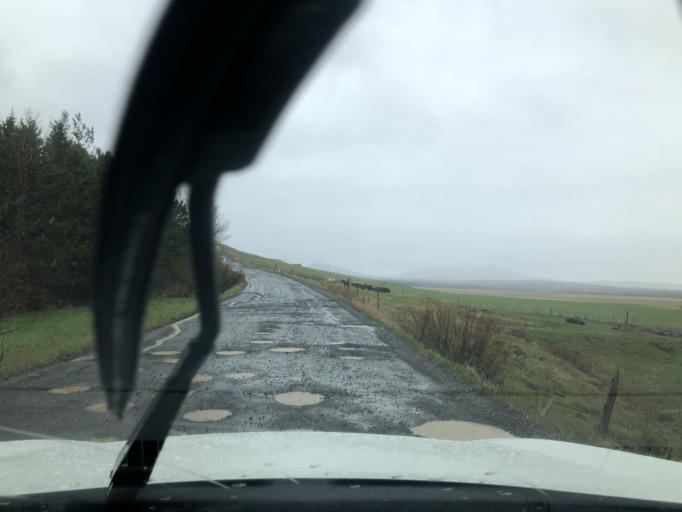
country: IS
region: South
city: Selfoss
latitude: 64.2394
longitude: -20.5502
